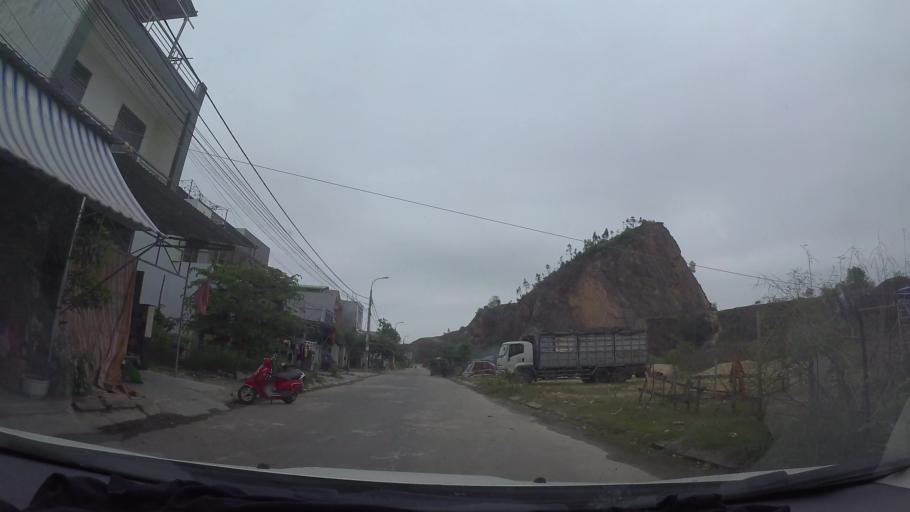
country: VN
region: Da Nang
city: Lien Chieu
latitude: 16.0658
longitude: 108.1445
